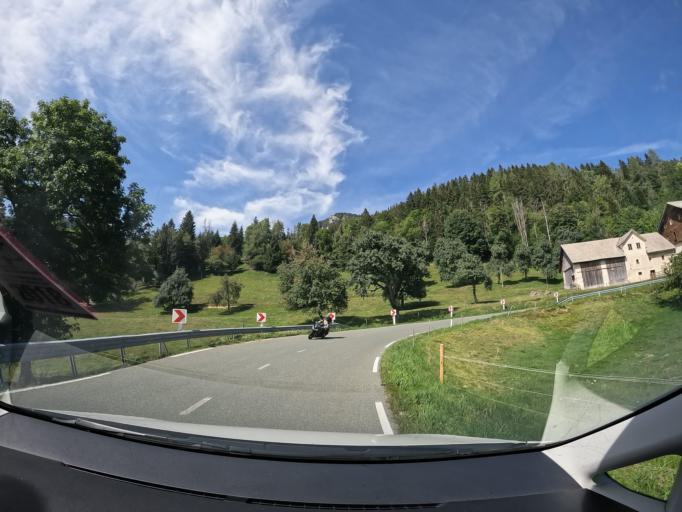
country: AT
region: Carinthia
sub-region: Politischer Bezirk Feldkirchen
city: Glanegg
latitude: 46.7419
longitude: 14.1769
